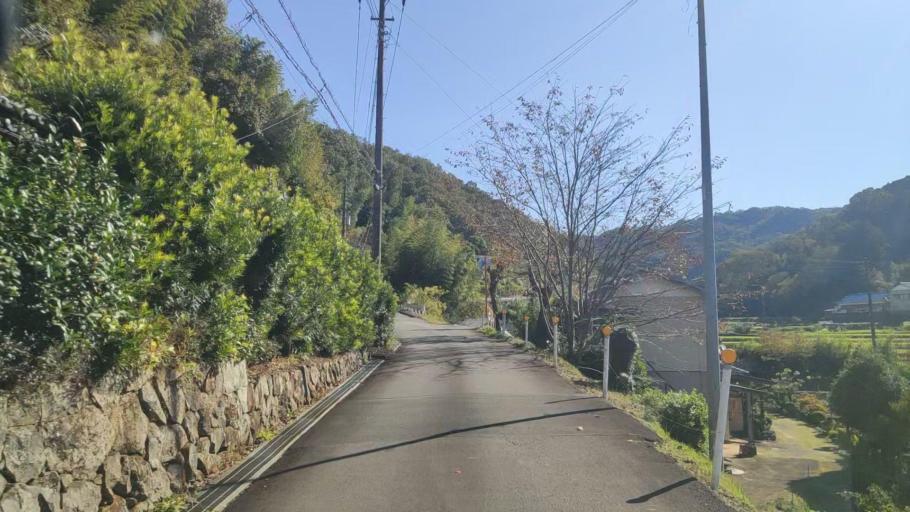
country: JP
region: Shizuoka
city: Mishima
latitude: 35.0173
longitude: 138.9530
